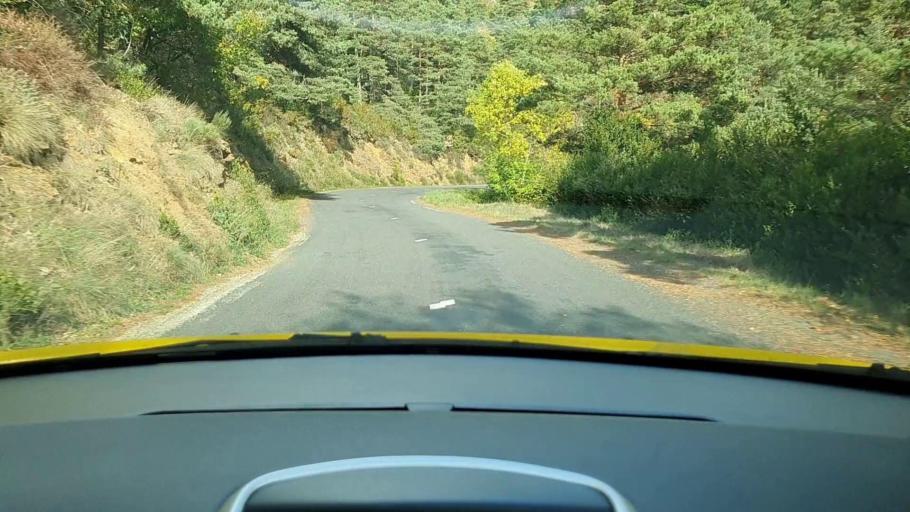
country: FR
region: Languedoc-Roussillon
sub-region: Departement de la Lozere
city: Meyrueis
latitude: 44.0694
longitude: 3.4126
